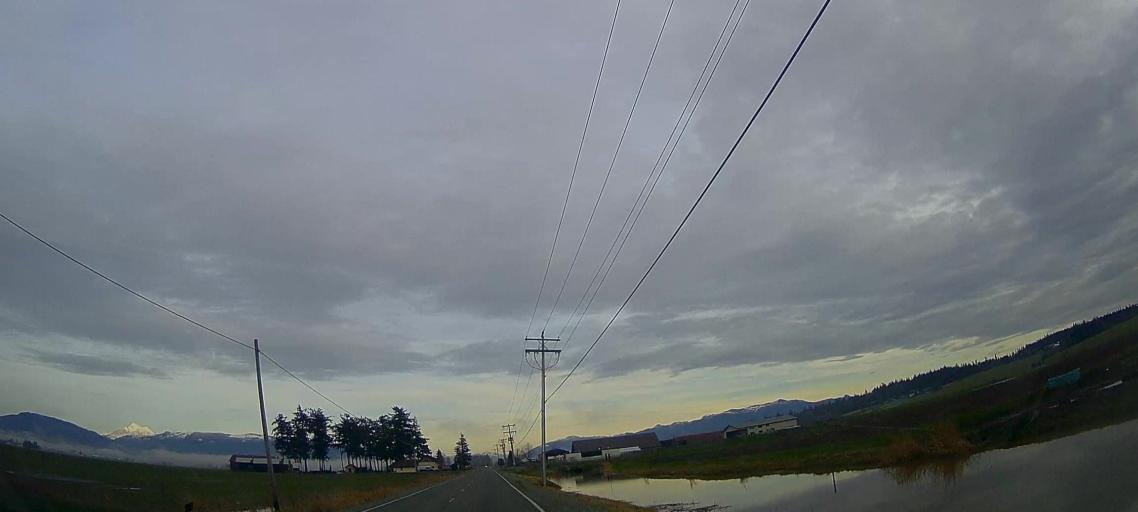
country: US
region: Washington
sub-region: Skagit County
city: Burlington
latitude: 48.5201
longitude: -122.4613
